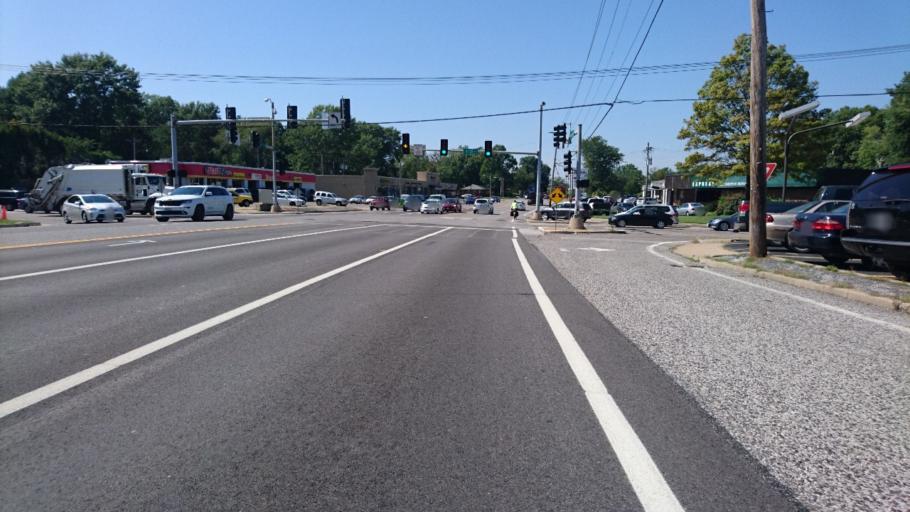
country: US
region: Missouri
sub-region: Saint Louis County
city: Des Peres
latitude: 38.5989
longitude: -90.4154
